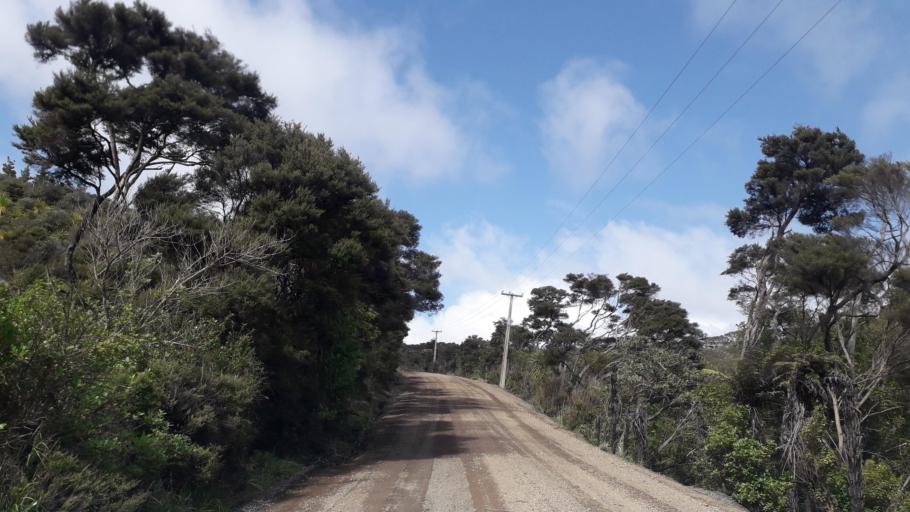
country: NZ
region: Northland
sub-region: Far North District
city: Paihia
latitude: -35.2406
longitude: 174.2481
